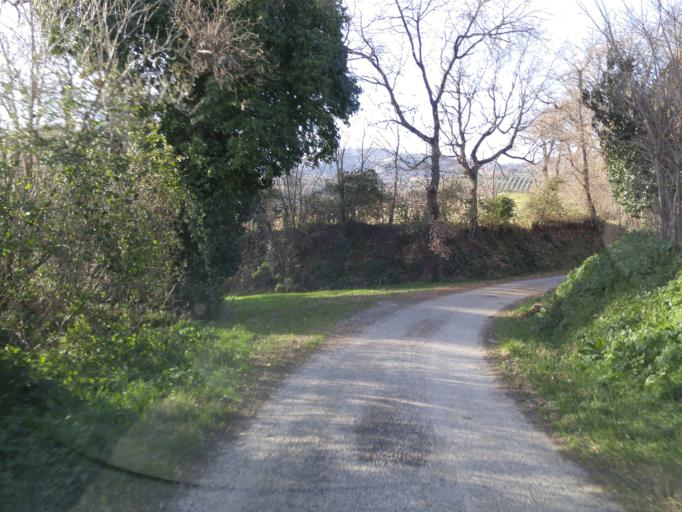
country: IT
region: The Marches
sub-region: Provincia di Pesaro e Urbino
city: Cartoceto
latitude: 43.7737
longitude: 12.8910
